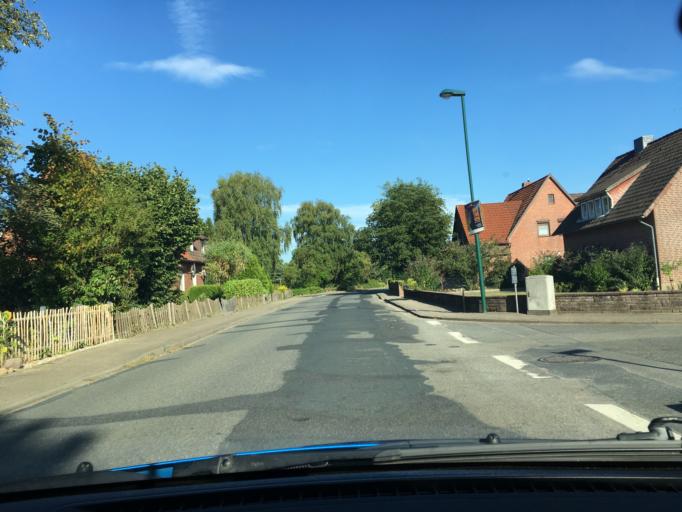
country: DE
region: Lower Saxony
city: Dahlenburg
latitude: 53.1912
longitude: 10.7255
